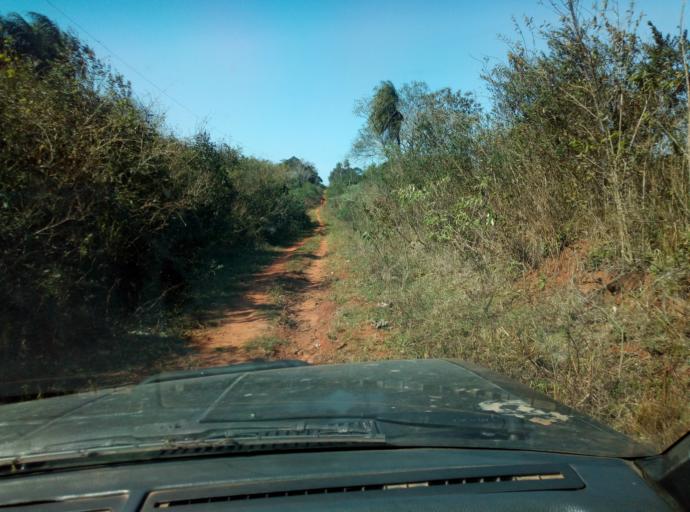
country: PY
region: Caaguazu
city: Doctor Cecilio Baez
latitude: -25.1793
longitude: -56.2165
